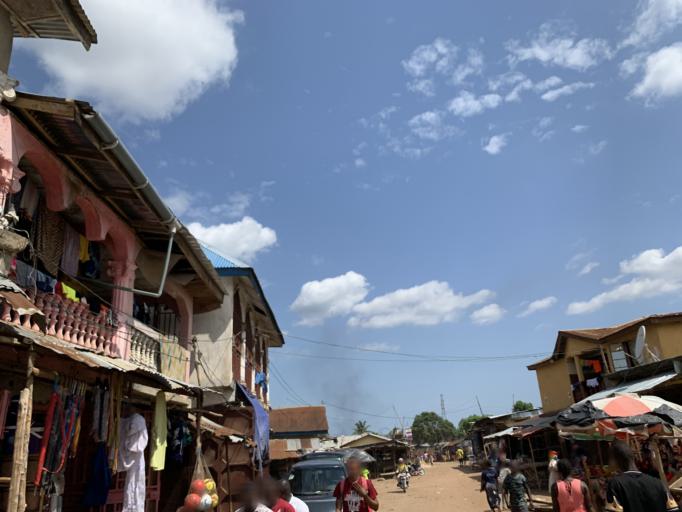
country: SL
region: Western Area
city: Waterloo
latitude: 8.3282
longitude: -13.0519
